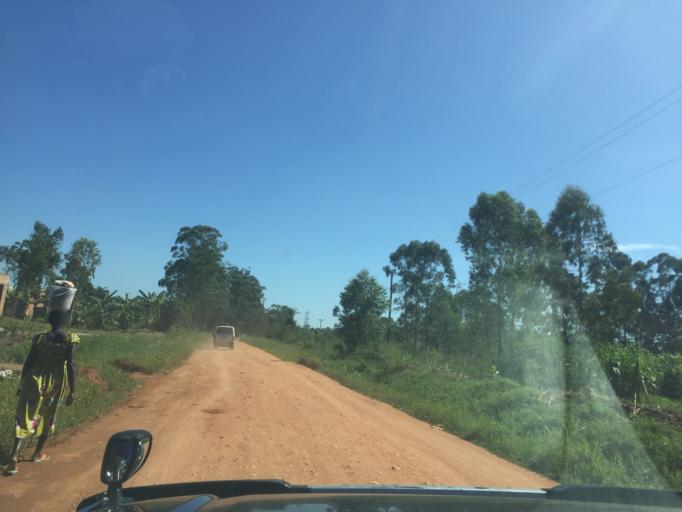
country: UG
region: Central Region
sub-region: Luwero District
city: Luwero
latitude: 0.8430
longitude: 32.5079
